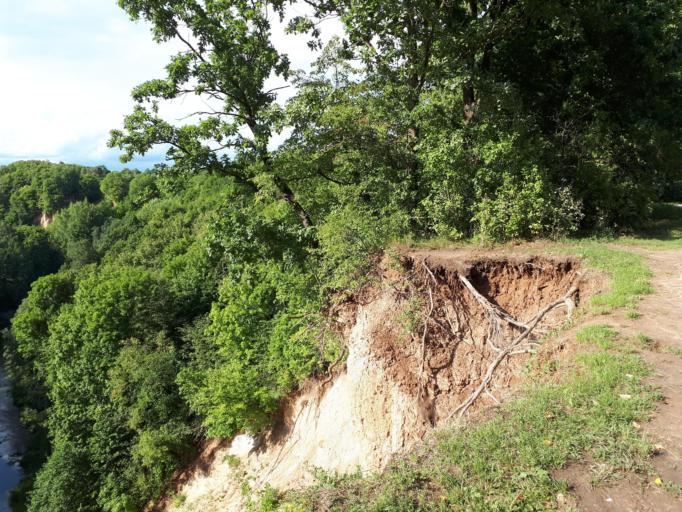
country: LT
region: Kauno apskritis
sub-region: Kaunas
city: Aleksotas
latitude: 54.8450
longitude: 23.9367
